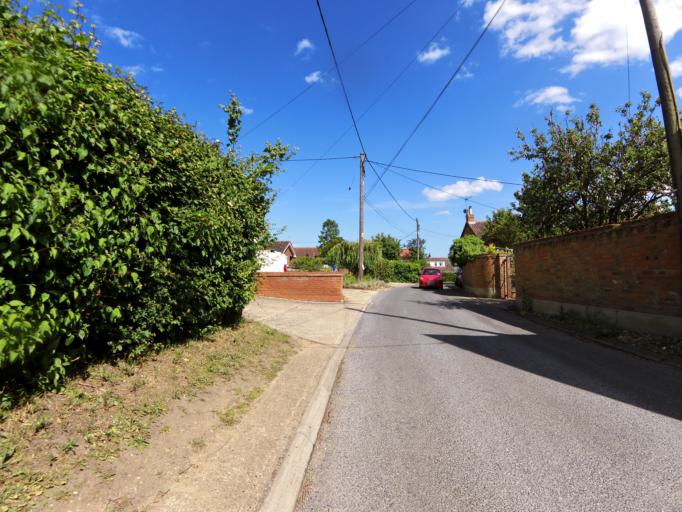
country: GB
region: England
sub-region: Suffolk
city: Shotley Gate
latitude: 52.0062
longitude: 1.2513
